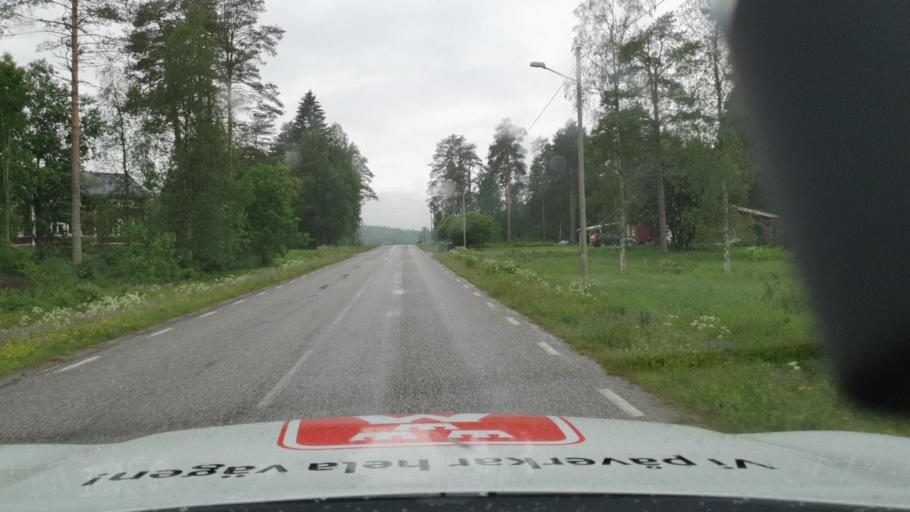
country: SE
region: Vaesterbotten
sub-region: Nordmalings Kommun
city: Nordmaling
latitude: 63.7939
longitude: 19.5341
